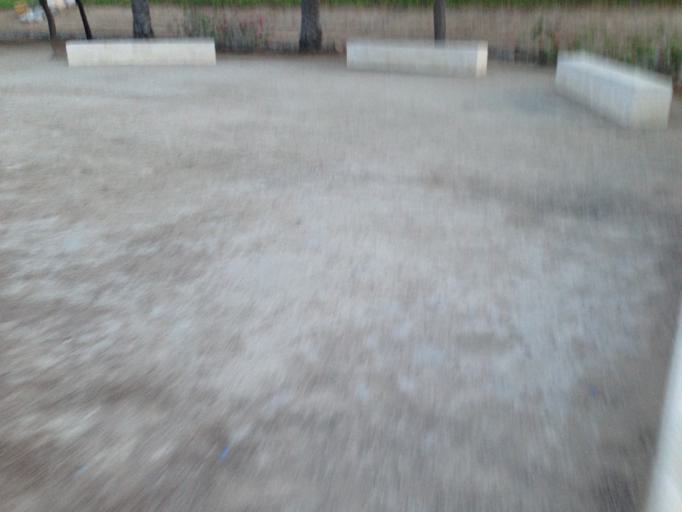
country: OM
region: Muhafazat Masqat
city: As Sib al Jadidah
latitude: 23.6240
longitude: 58.2670
